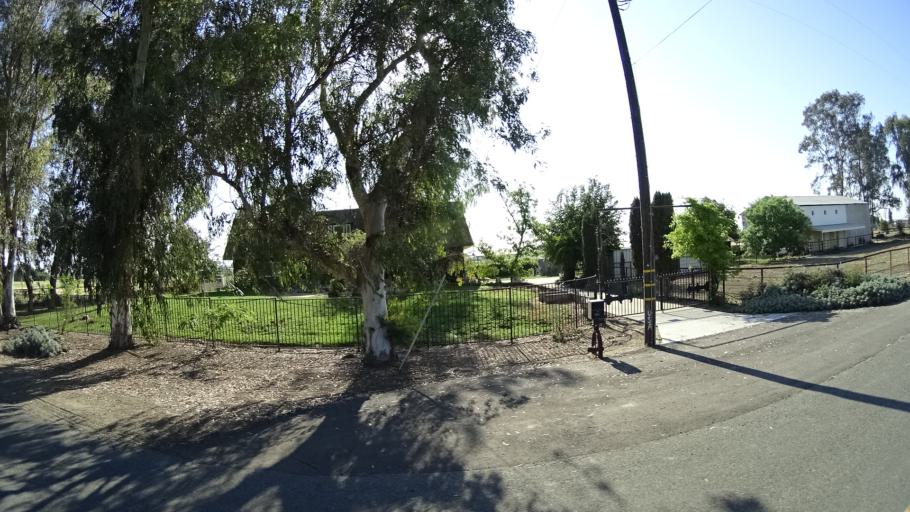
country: US
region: California
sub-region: Fresno County
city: Riverdale
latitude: 36.3546
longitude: -119.8693
